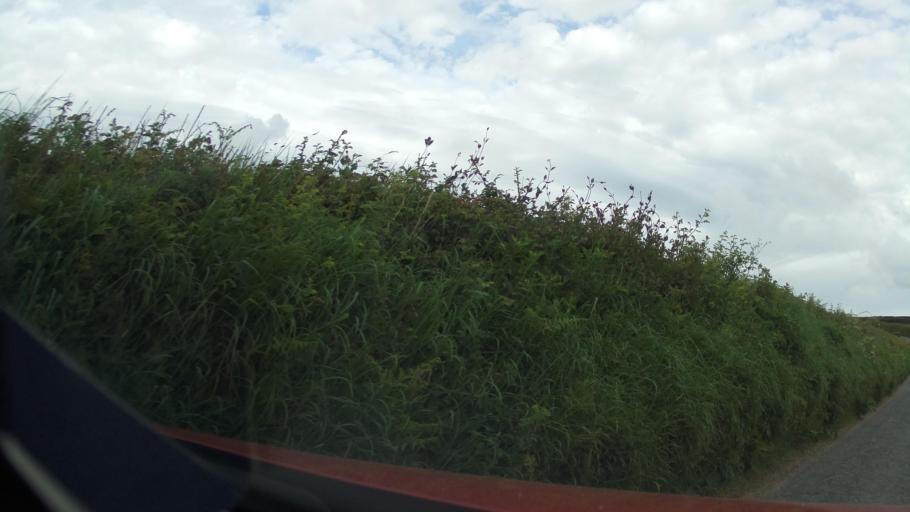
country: GB
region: England
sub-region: Devon
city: Dartmouth
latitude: 50.3243
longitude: -3.6391
